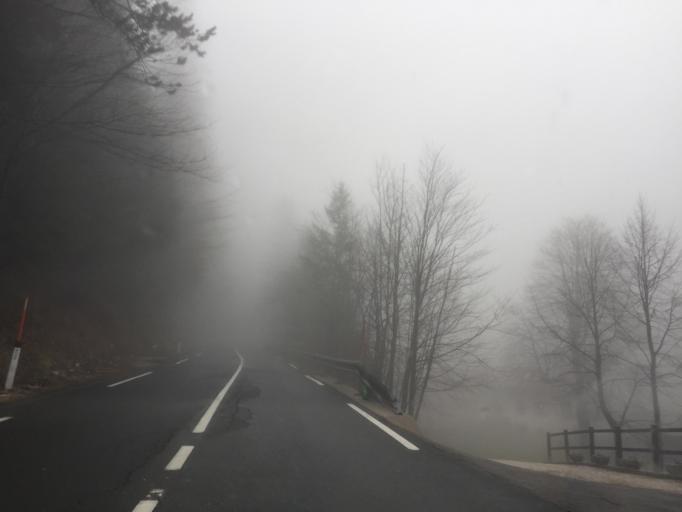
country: SI
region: Ajdovscina
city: Lokavec
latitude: 45.9447
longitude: 13.8720
